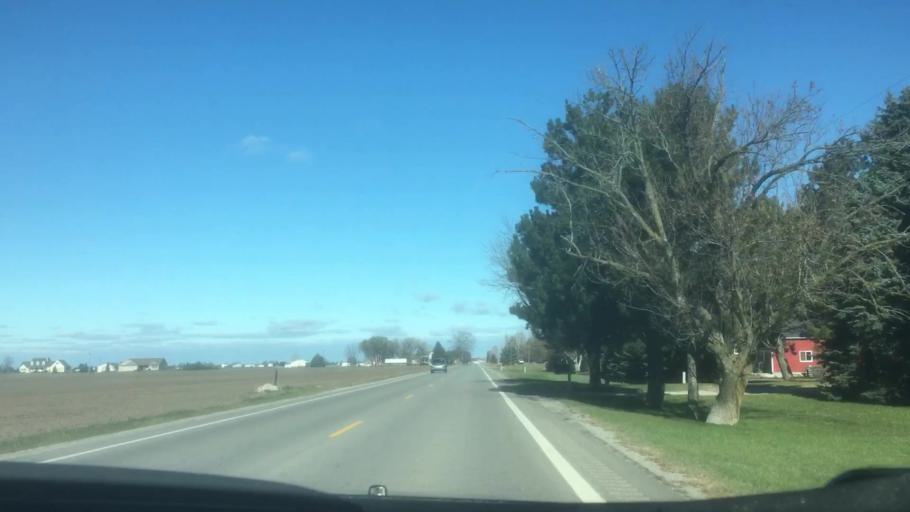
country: US
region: Michigan
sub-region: Bay County
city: Essexville
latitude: 43.5470
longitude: -83.7589
